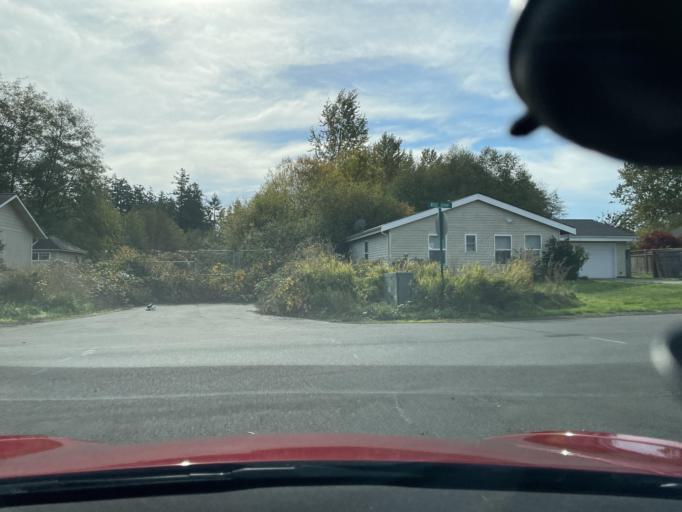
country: US
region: Washington
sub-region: San Juan County
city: Friday Harbor
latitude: 48.5270
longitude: -123.0215
